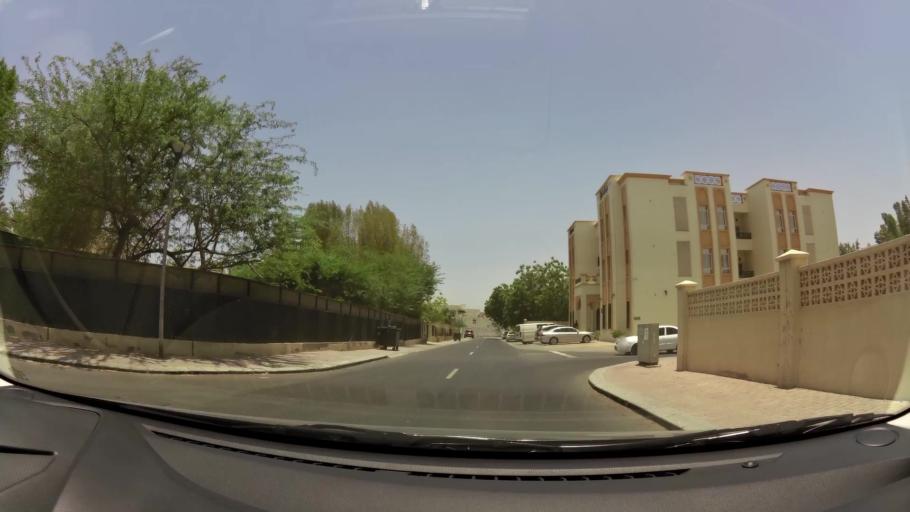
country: OM
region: Muhafazat Masqat
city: Bawshar
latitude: 23.5999
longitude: 58.4584
